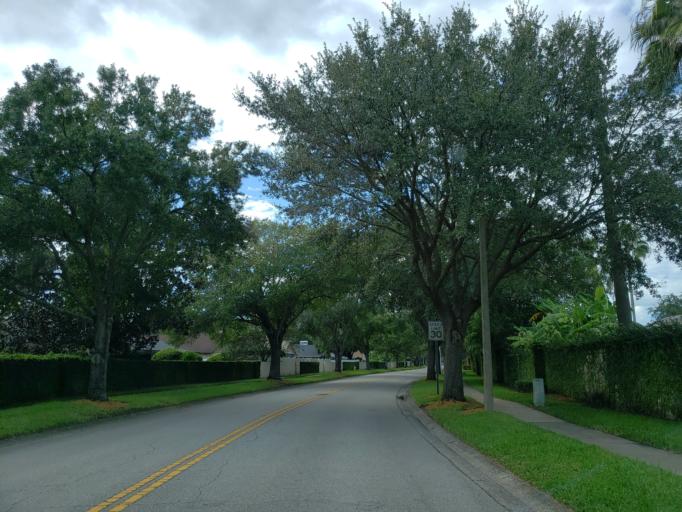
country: US
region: Florida
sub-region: Hillsborough County
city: Bloomingdale
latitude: 27.8732
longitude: -82.2555
